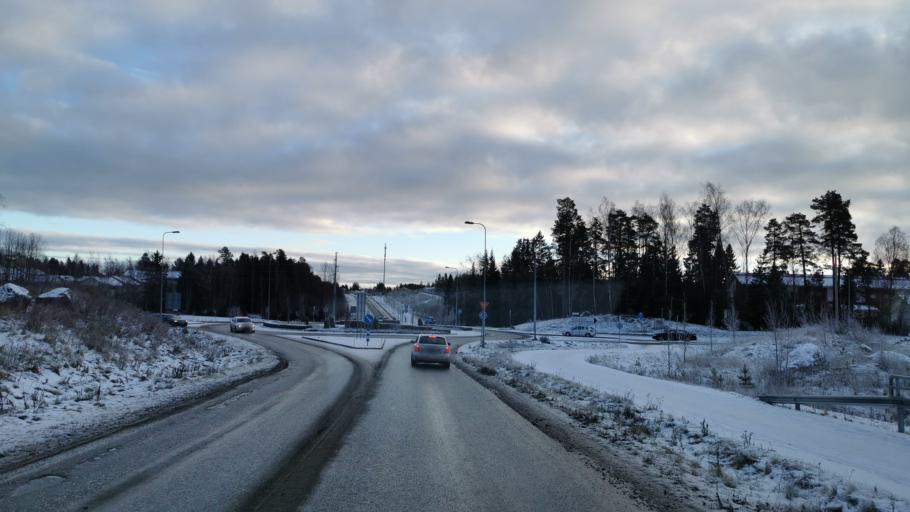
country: FI
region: Ostrobothnia
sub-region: Vaasa
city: Korsholm
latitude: 63.1102
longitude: 21.6642
